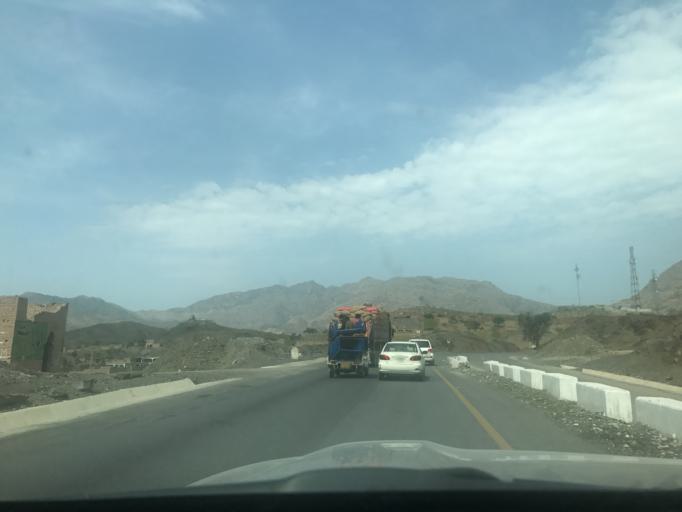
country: PK
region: Federally Administered Tribal Areas
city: Landi Kotal
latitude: 34.0085
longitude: 71.2880
